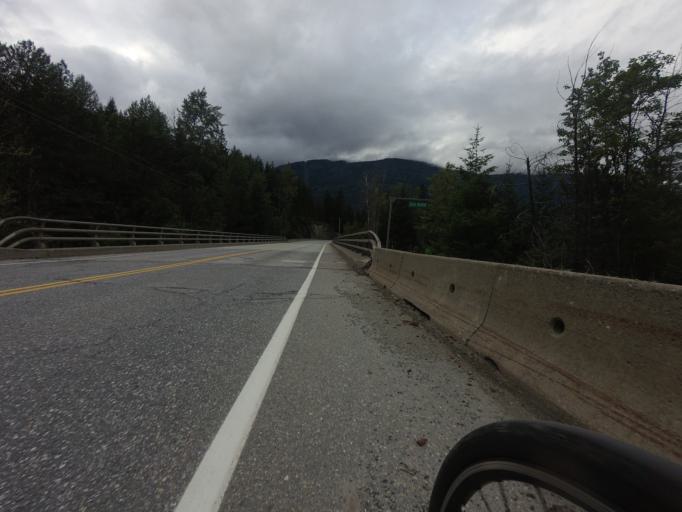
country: CA
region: British Columbia
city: Pemberton
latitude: 50.2580
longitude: -122.8633
